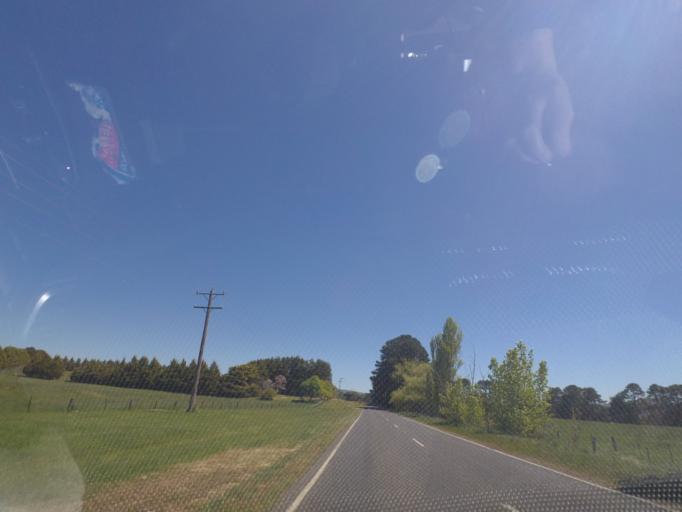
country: AU
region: Victoria
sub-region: Hume
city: Sunbury
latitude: -37.2797
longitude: 144.7483
